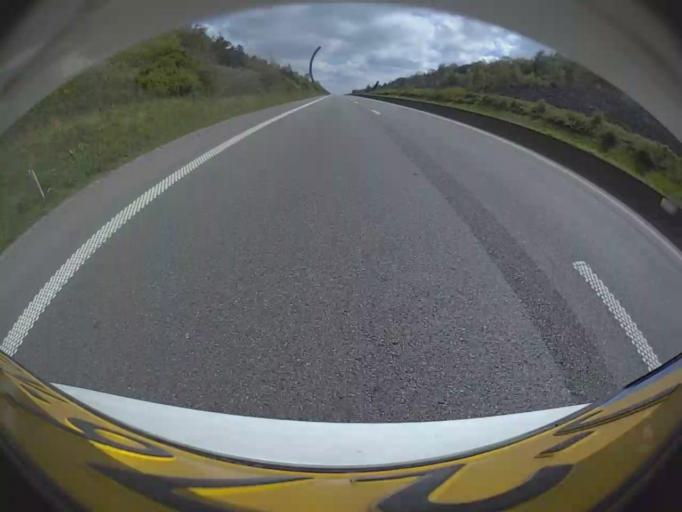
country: BE
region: Wallonia
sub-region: Province du Luxembourg
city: Wellin
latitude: 50.1129
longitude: 5.1085
